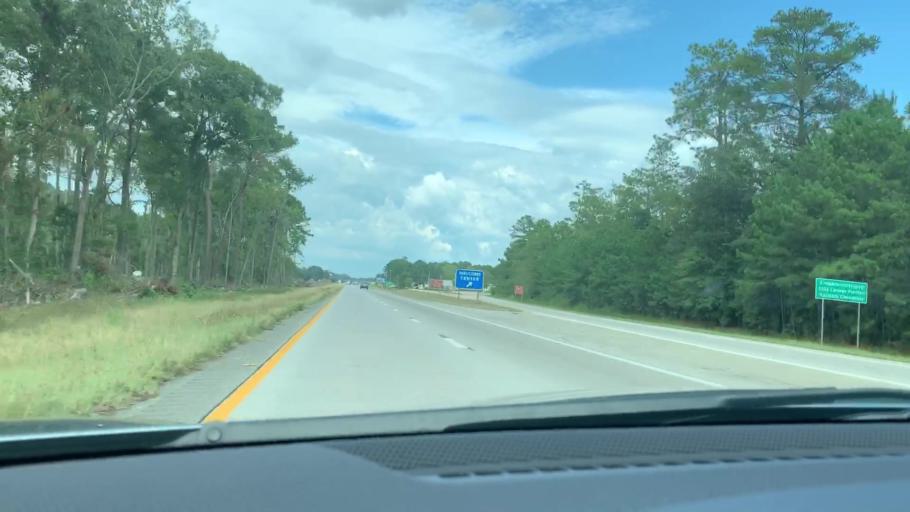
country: US
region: South Carolina
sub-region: Jasper County
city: Hardeeville
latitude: 32.2633
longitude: -81.0913
